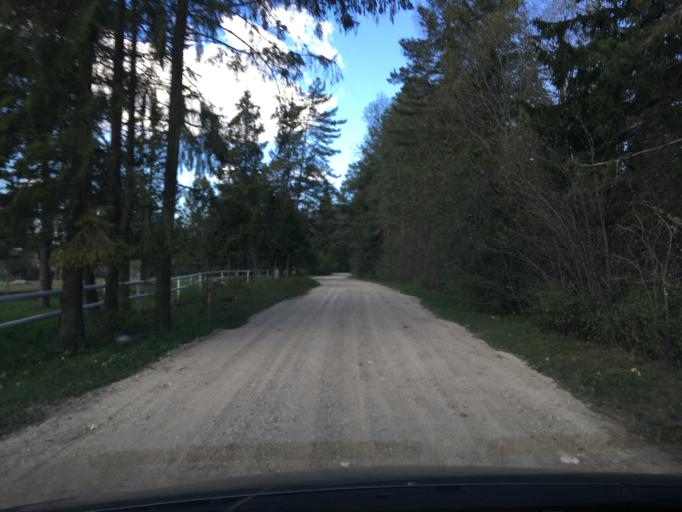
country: EE
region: Harju
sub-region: Raasiku vald
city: Raasiku
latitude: 59.2117
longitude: 25.1706
